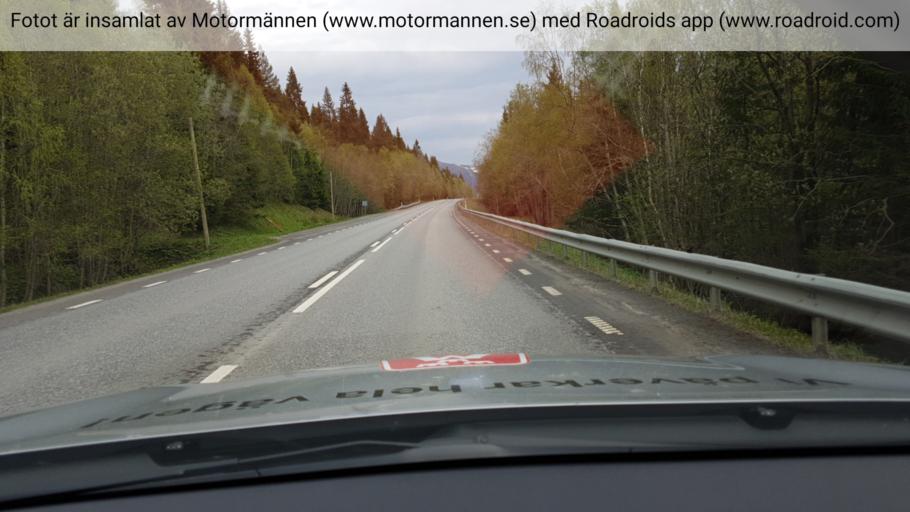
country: SE
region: Jaemtland
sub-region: Are Kommun
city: Are
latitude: 63.4023
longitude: 12.9926
